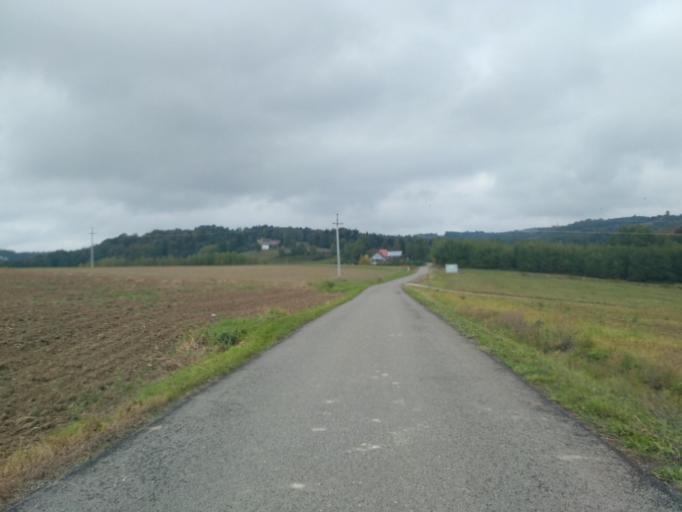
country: PL
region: Subcarpathian Voivodeship
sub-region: Powiat debicki
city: Brzostek
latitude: 49.9404
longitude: 21.4519
